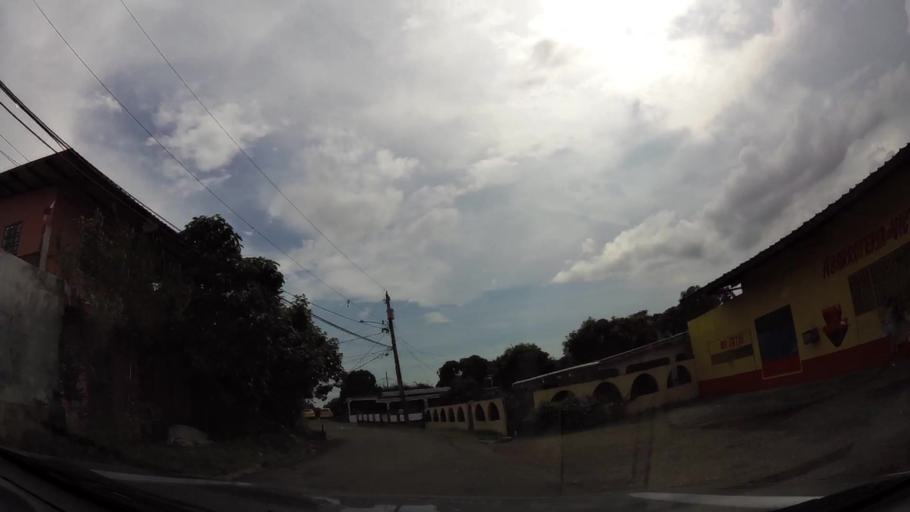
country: PA
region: Panama
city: Tocumen
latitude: 9.0991
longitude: -79.3674
